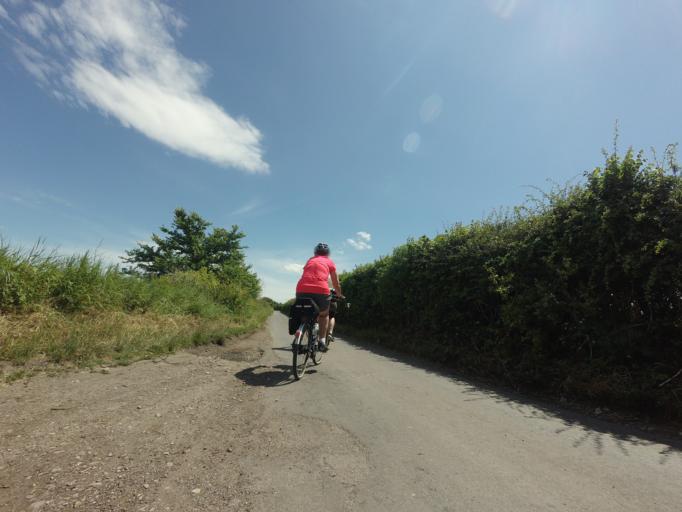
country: GB
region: England
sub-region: Kent
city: Cliffe
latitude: 51.4613
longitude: 0.5096
